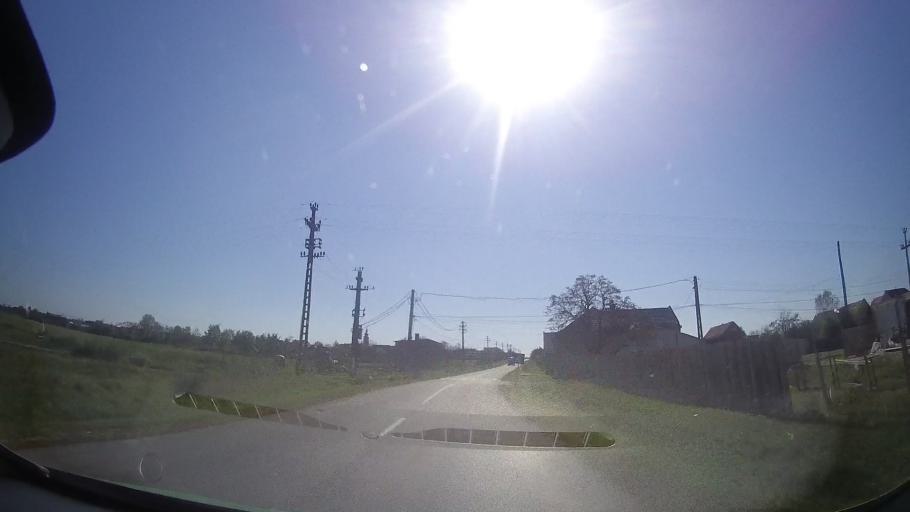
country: RO
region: Timis
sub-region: Comuna Bethausen
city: Bethausen
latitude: 45.7979
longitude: 21.9642
